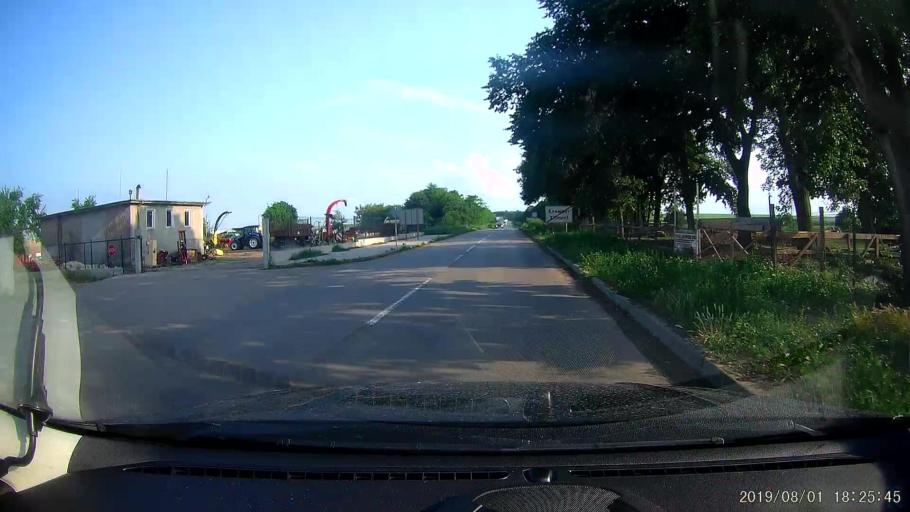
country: BG
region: Shumen
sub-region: Obshtina Venets
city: Venets
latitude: 43.6131
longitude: 26.9955
